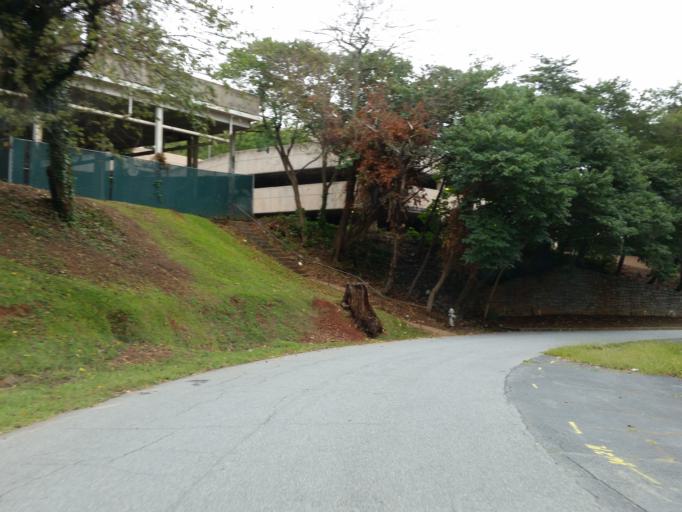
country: US
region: Georgia
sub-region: Cobb County
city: Marietta
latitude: 33.9701
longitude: -84.5497
